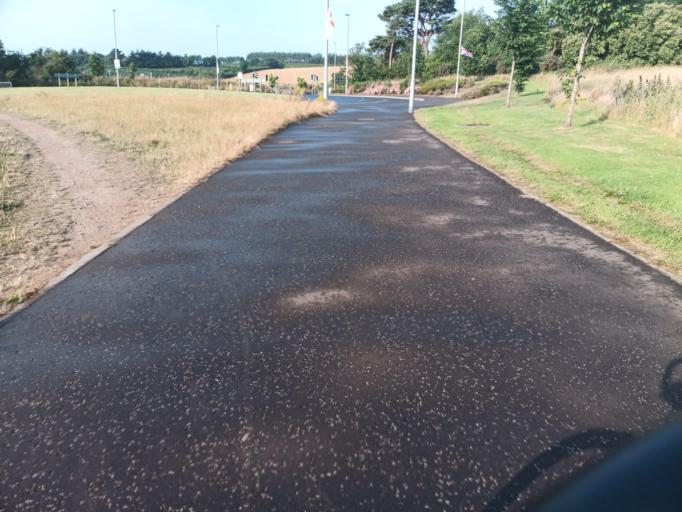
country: GB
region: Northern Ireland
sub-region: Castlereagh District
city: Dundonald
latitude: 54.5831
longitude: -5.7906
